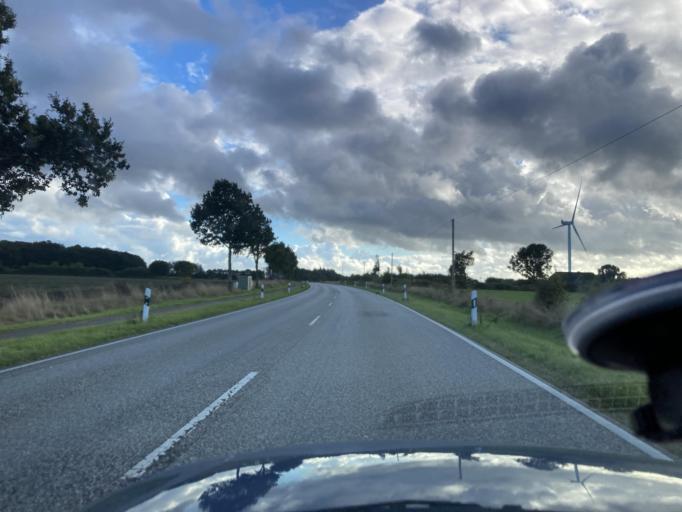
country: DE
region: Schleswig-Holstein
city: Hamdorf
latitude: 54.2479
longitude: 9.5300
